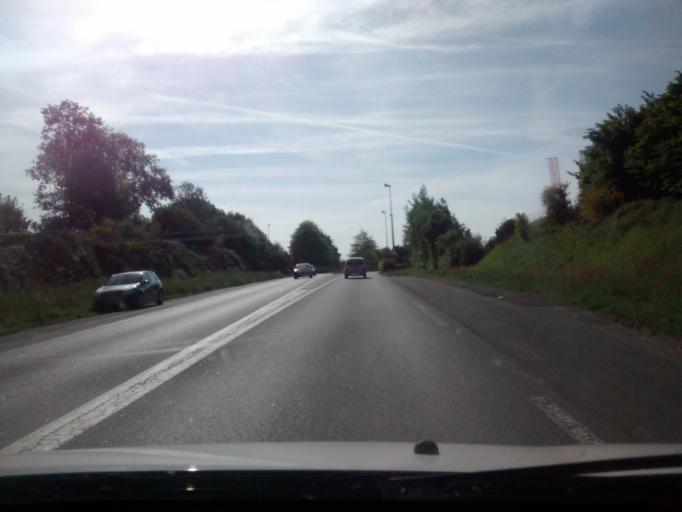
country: FR
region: Brittany
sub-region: Departement d'Ille-et-Vilaine
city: Fougeres
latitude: 48.3393
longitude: -1.2131
